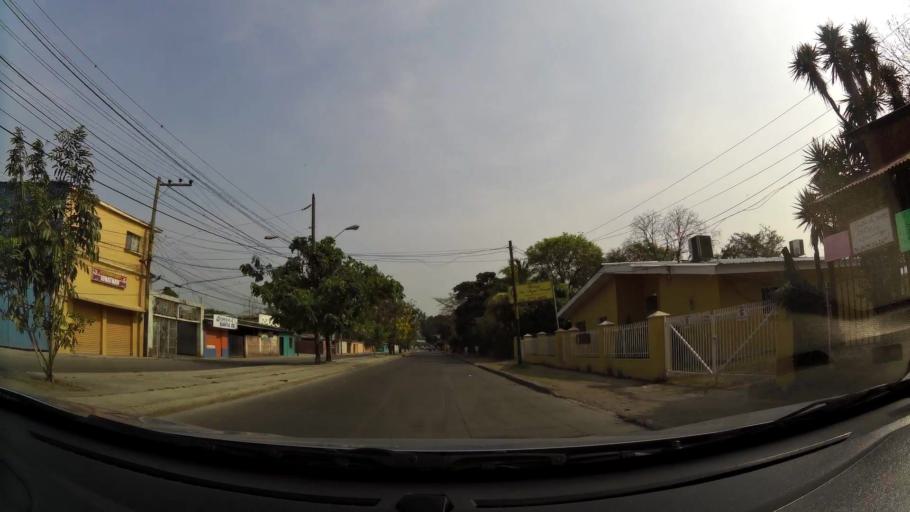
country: HN
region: Comayagua
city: Comayagua
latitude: 14.4626
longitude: -87.6455
